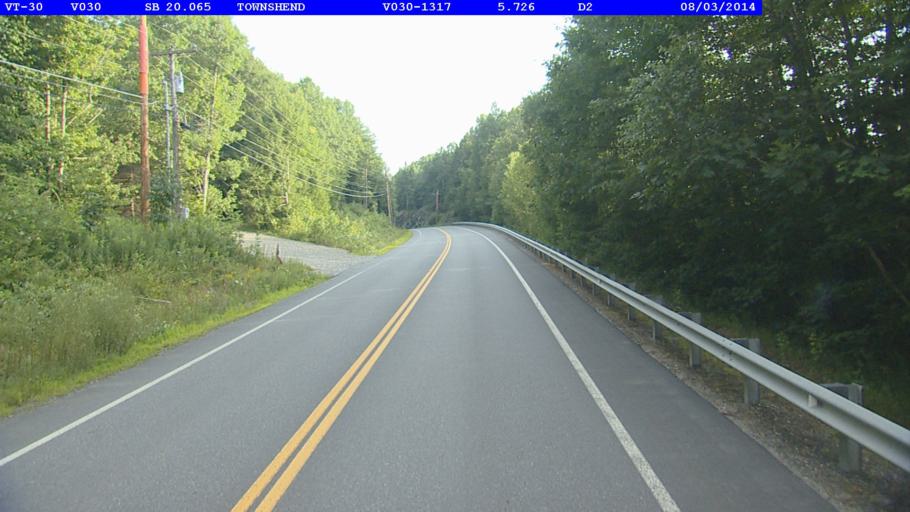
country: US
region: Vermont
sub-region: Windham County
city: Newfane
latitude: 43.0747
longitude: -72.7048
